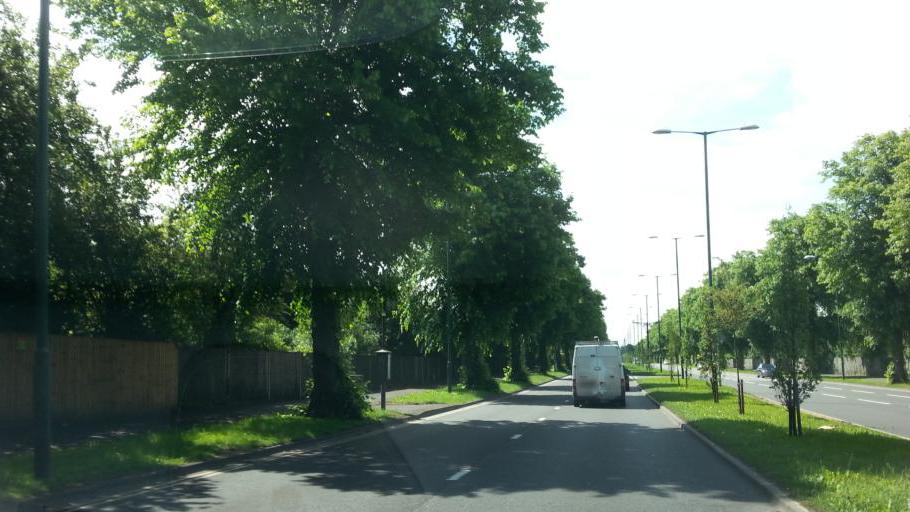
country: GB
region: England
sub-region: Nottingham
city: Nottingham
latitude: 52.9672
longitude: -1.1905
